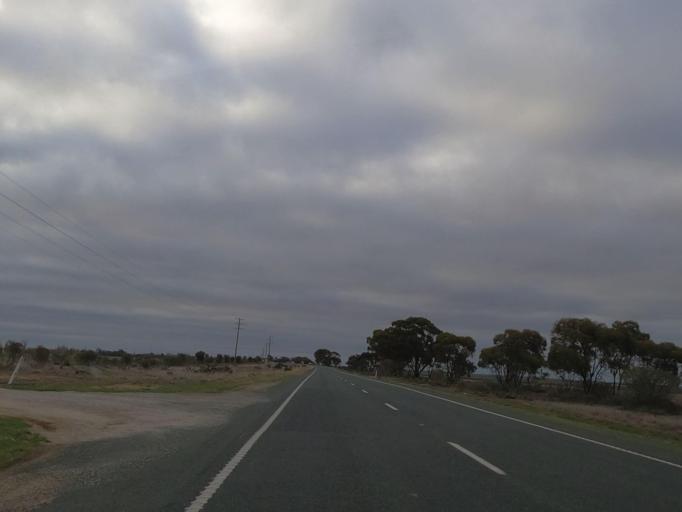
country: AU
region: Victoria
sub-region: Swan Hill
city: Swan Hill
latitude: -35.5782
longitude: 143.7886
